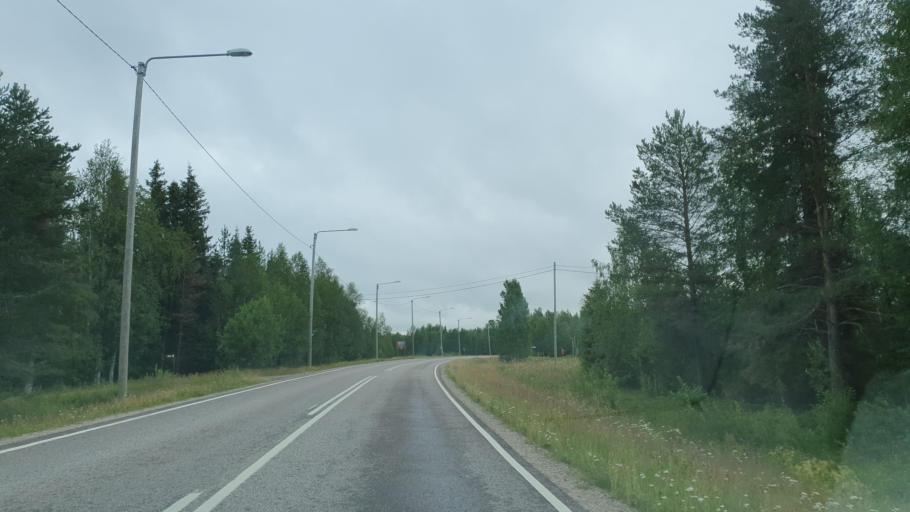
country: FI
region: Lapland
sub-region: Itae-Lappi
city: Pelkosenniemi
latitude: 66.9813
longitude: 27.5283
